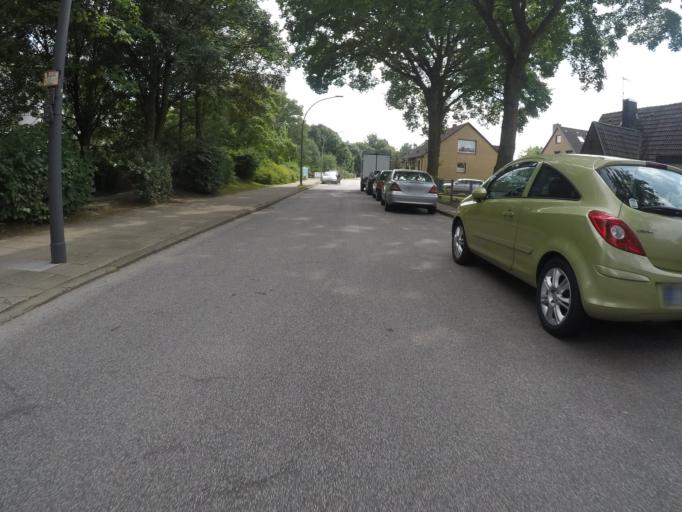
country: DE
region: Hamburg
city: Wandsbek
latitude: 53.5466
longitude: 10.1163
